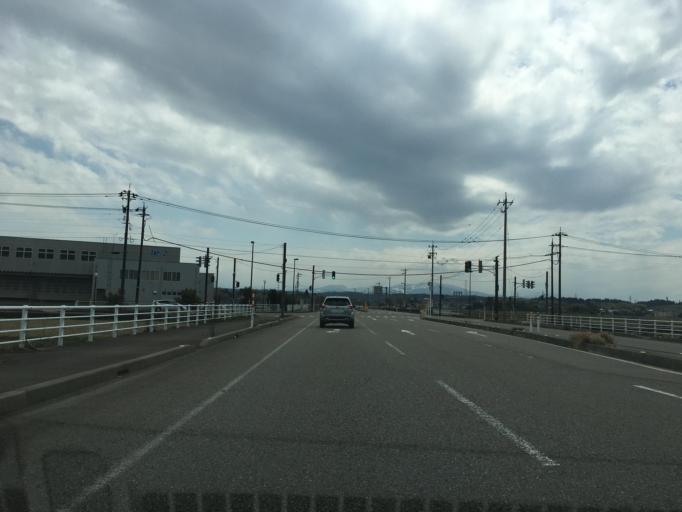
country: JP
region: Toyama
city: Kuragaki-kosugi
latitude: 36.7118
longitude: 137.1171
